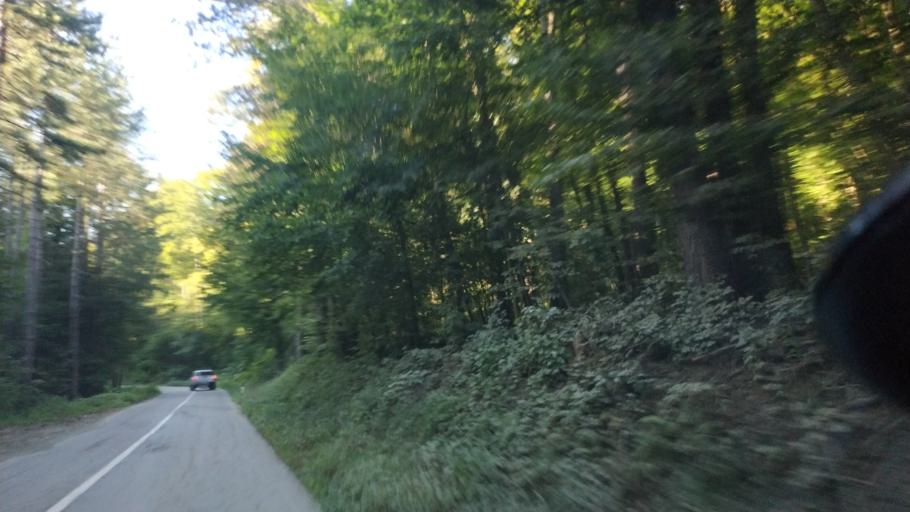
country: RS
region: Central Serbia
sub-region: Rasinski Okrug
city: Krusevac
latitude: 43.4522
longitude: 21.3595
